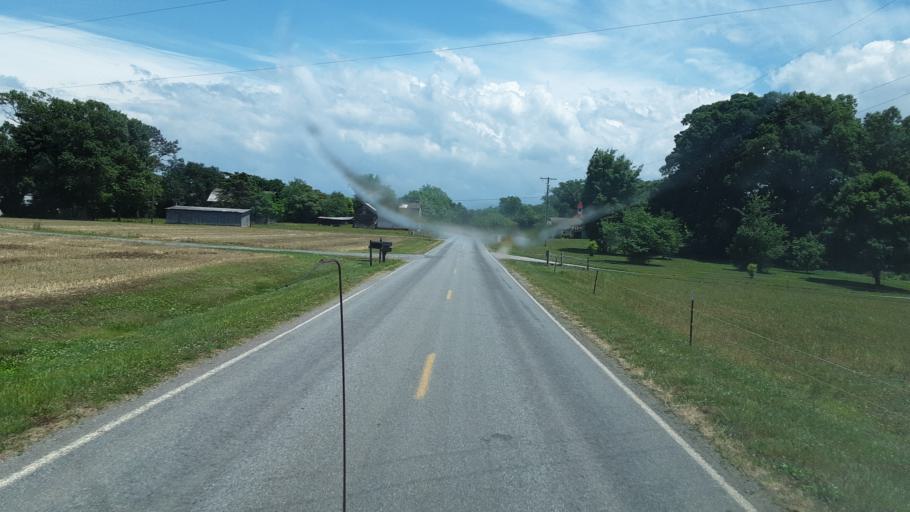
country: US
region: North Carolina
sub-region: Yadkin County
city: Jonesville
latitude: 36.0709
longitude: -80.8357
